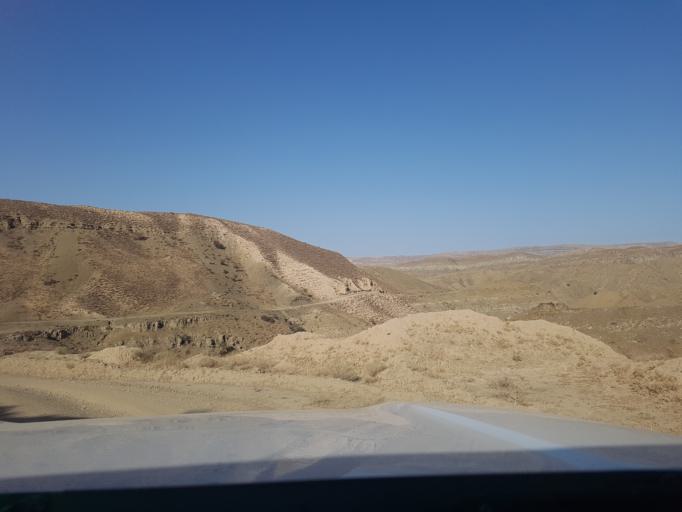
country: TM
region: Balkan
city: Magtymguly
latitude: 38.3010
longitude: 56.7820
